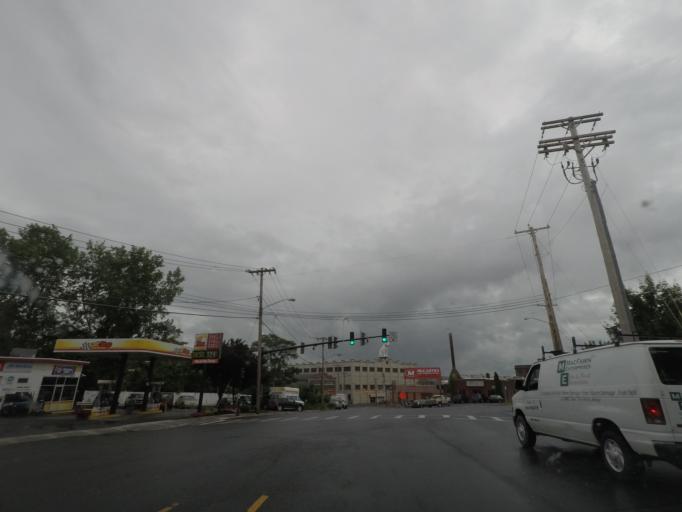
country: US
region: New York
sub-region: Albany County
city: Albany
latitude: 42.6657
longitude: -73.7435
